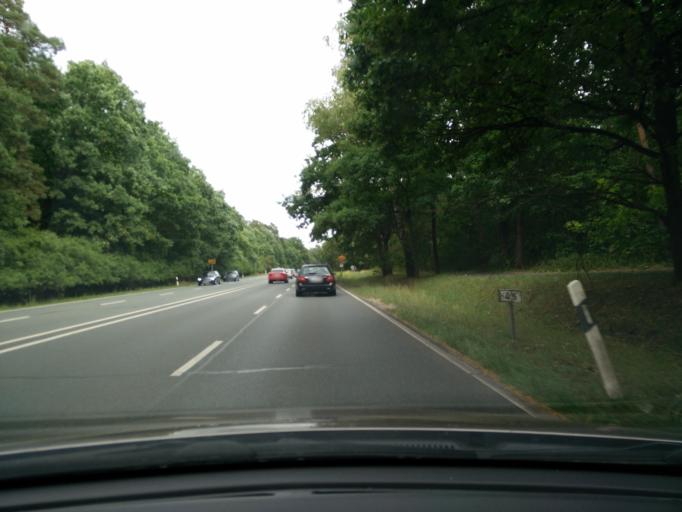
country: DE
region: Bavaria
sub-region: Regierungsbezirk Mittelfranken
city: Nuernberg
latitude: 49.4302
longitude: 11.1376
